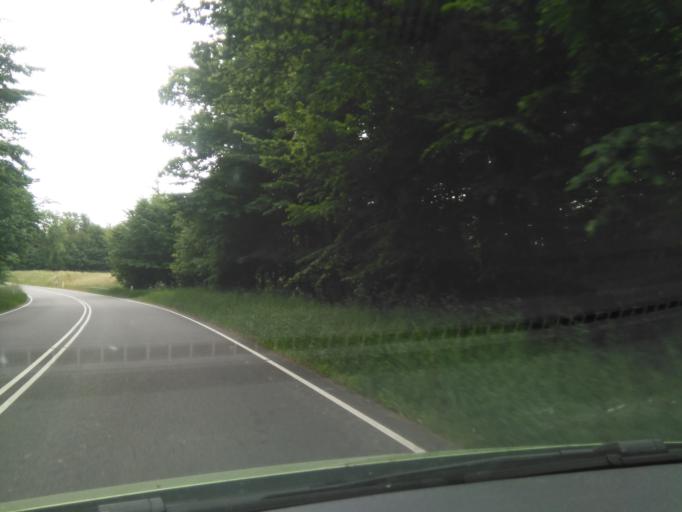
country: DK
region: Capital Region
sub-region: Bornholm Kommune
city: Akirkeby
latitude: 55.2312
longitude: 14.8773
